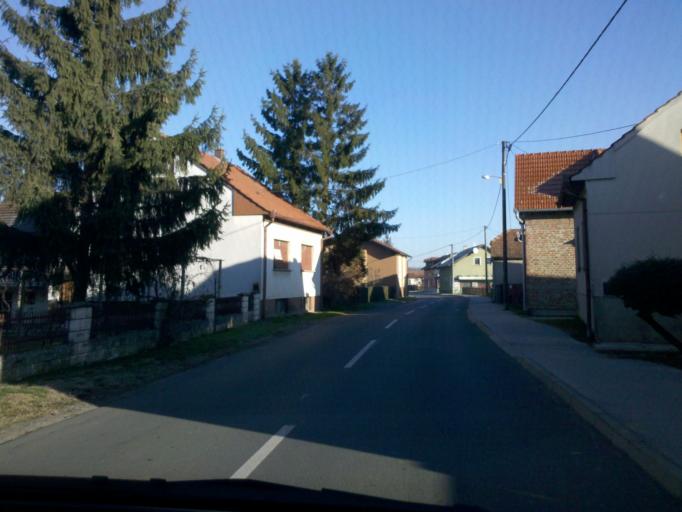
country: HR
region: Medimurska
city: Palovec
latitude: 46.3854
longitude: 16.5469
